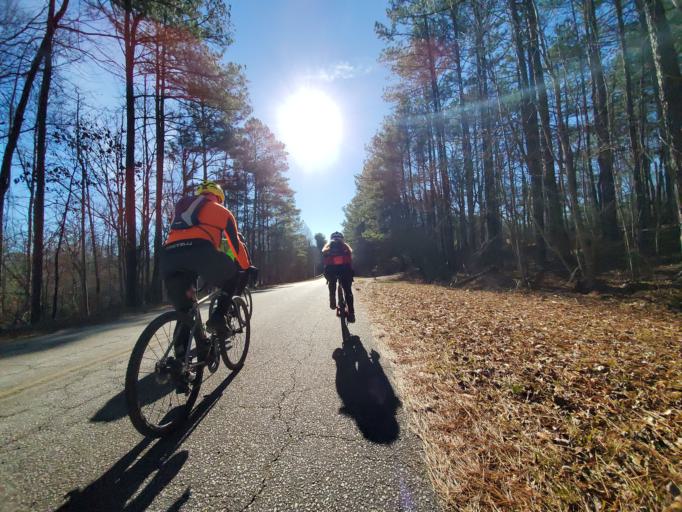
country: US
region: Georgia
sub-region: Fulton County
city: Chattahoochee Hills
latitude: 33.5675
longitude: -84.7878
